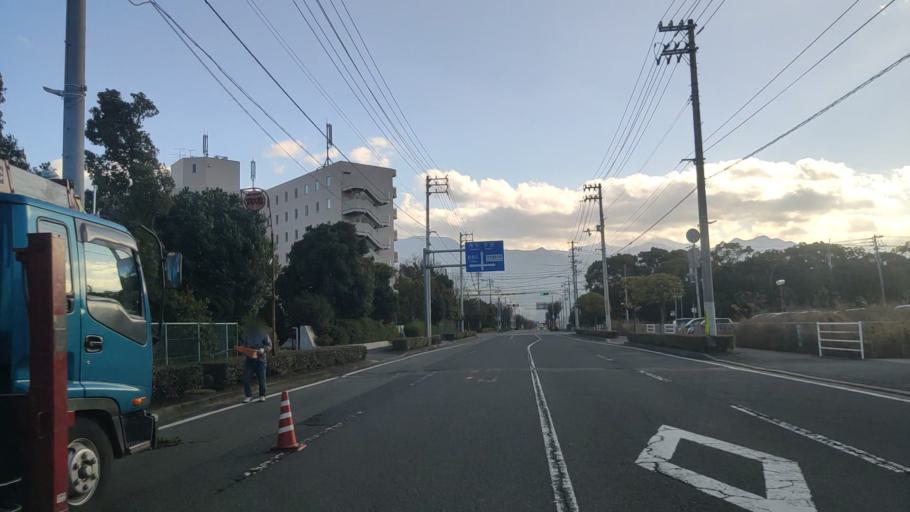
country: JP
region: Ehime
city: Saijo
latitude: 33.9364
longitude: 133.1922
